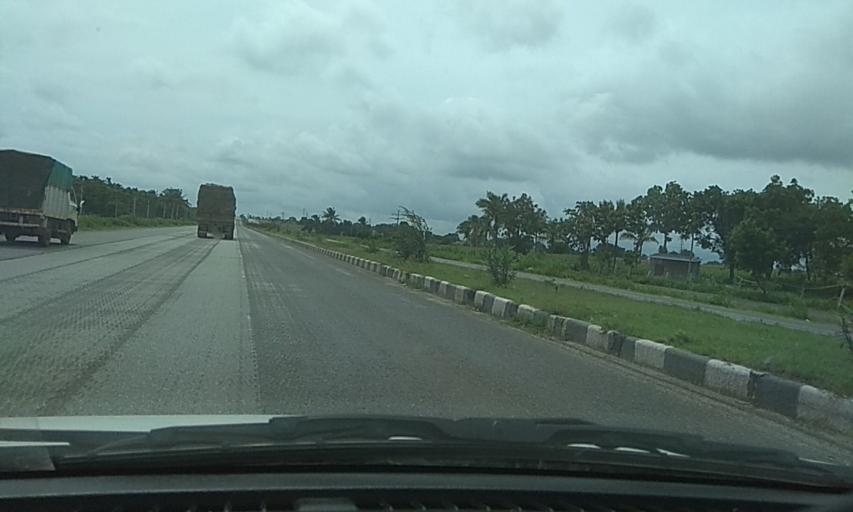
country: IN
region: Karnataka
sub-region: Davanagere
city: Mayakonda
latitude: 14.3335
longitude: 76.2168
